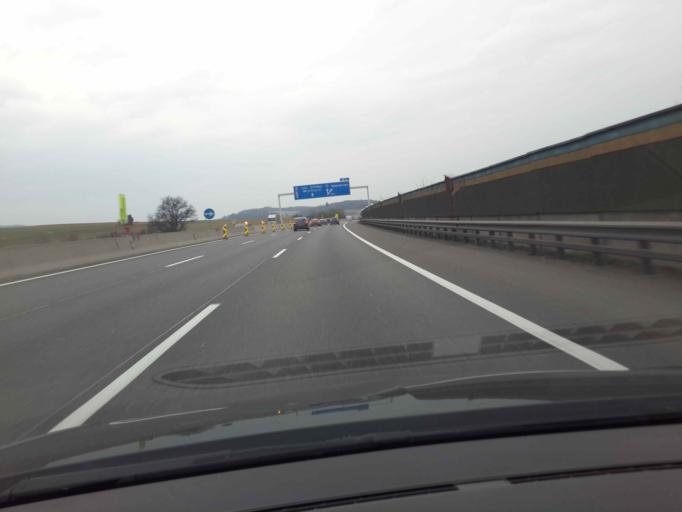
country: AT
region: Lower Austria
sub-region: Politischer Bezirk Sankt Polten
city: Boheimkirchen
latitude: 48.1842
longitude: 15.7760
